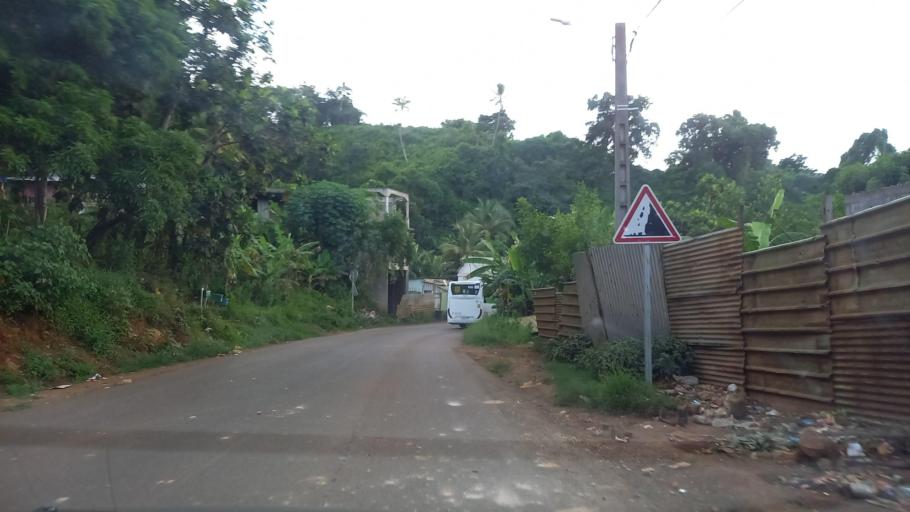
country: YT
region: M'Tsangamouji
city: M'Tsangamouji
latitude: -12.7604
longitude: 45.0887
